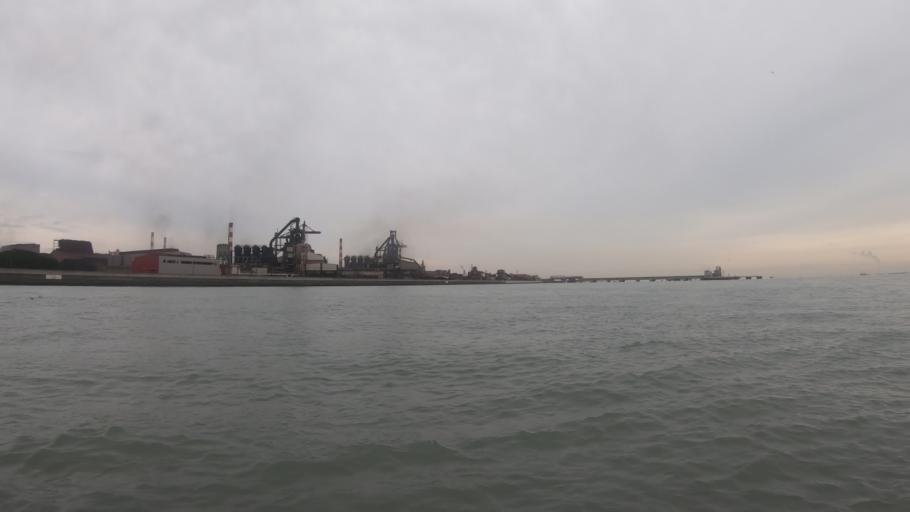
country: JP
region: Kanagawa
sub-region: Kawasaki-shi
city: Kawasaki
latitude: 35.4673
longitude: 139.7253
